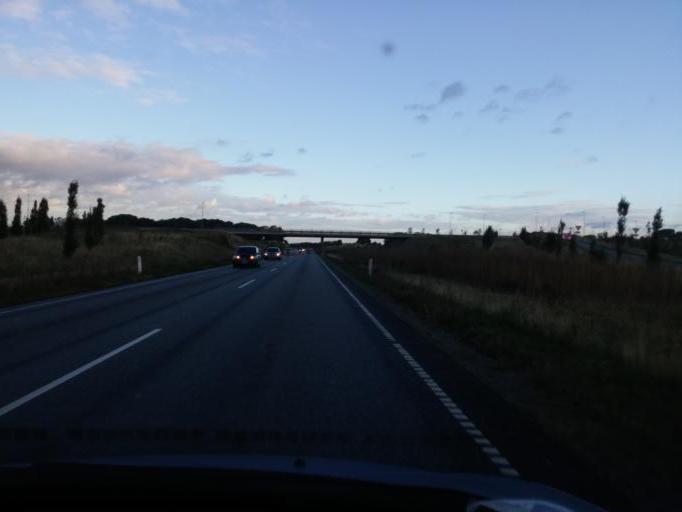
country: DK
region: South Denmark
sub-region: Odense Kommune
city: Bullerup
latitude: 55.4063
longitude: 10.4732
